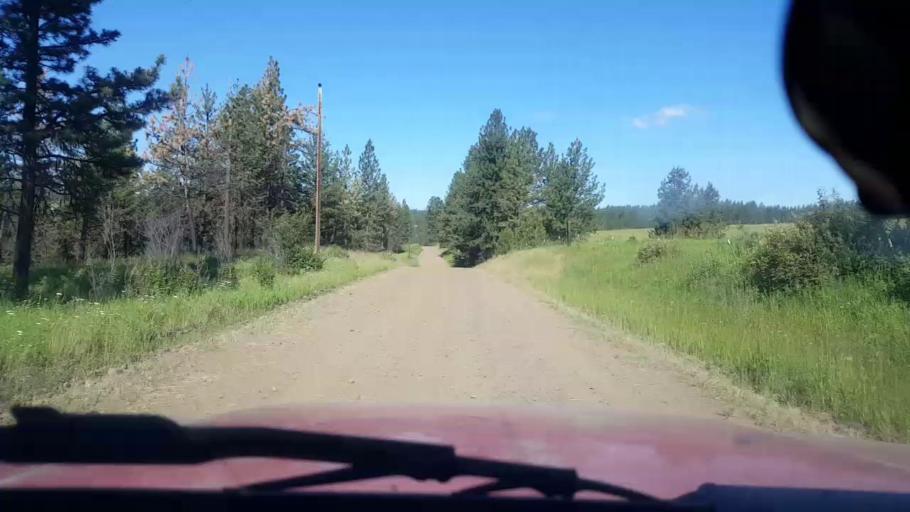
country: US
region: Washington
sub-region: Garfield County
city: Pomeroy
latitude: 45.9845
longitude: -117.4737
